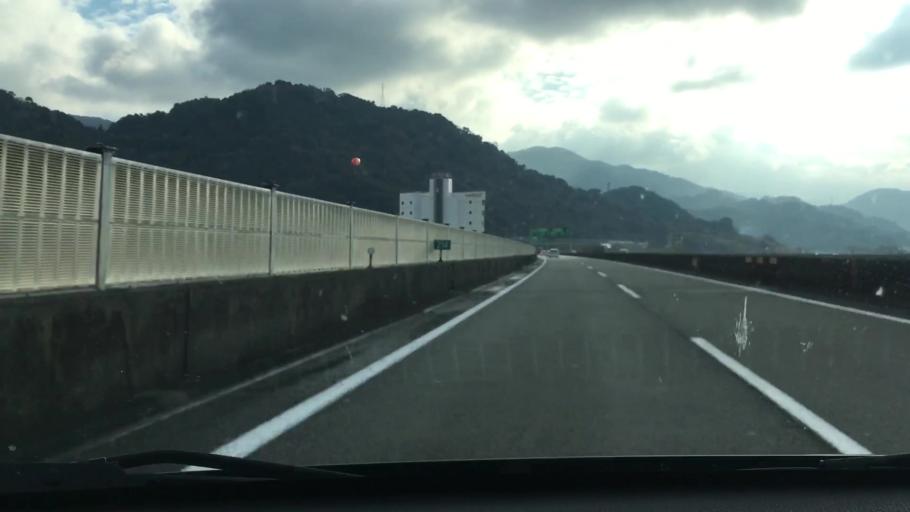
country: JP
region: Kumamoto
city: Yatsushiro
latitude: 32.5091
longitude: 130.6467
